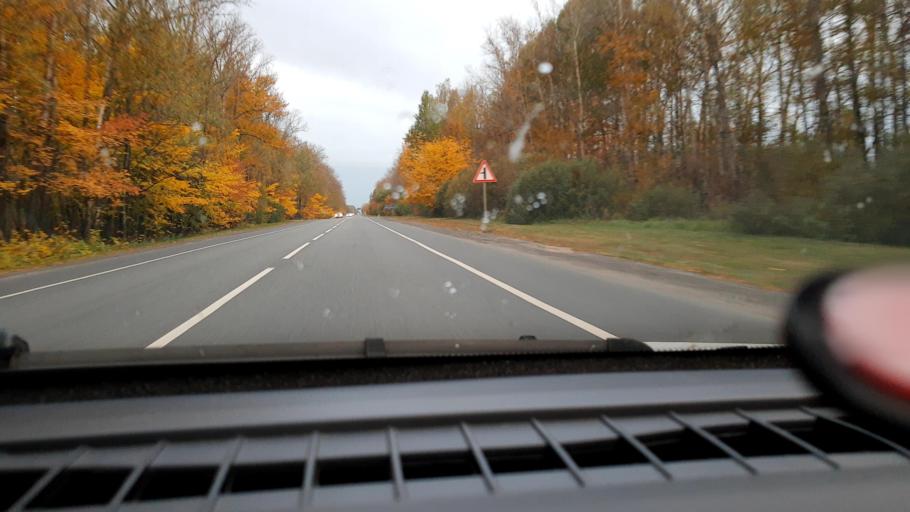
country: RU
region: Vladimir
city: Orgtrud
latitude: 56.2021
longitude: 40.7781
